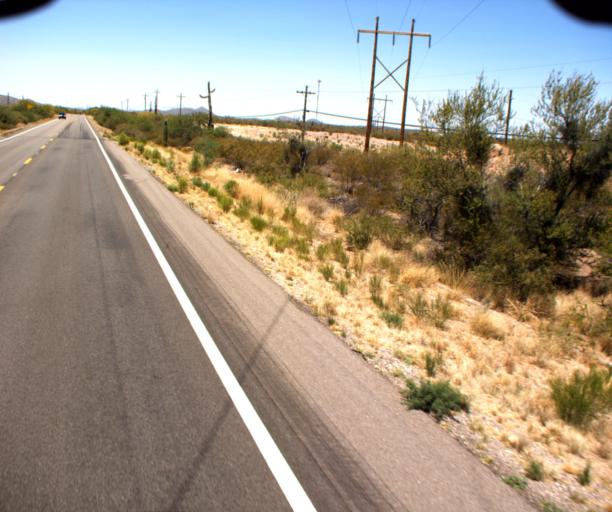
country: US
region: Arizona
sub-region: Pima County
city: Catalina
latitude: 32.6722
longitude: -111.0620
